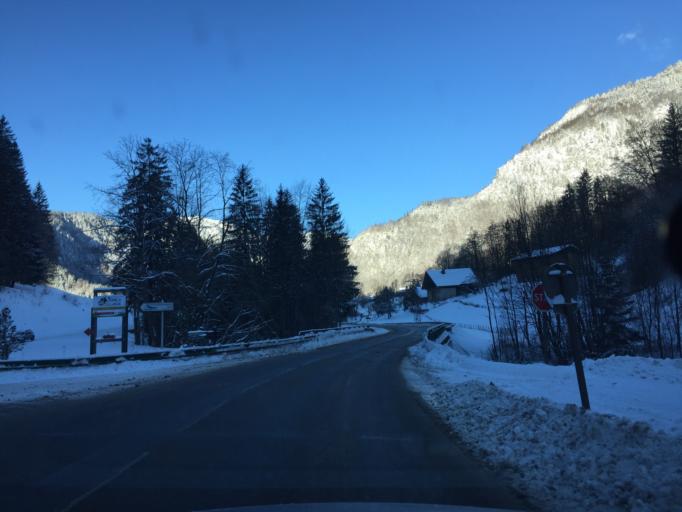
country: FR
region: Rhone-Alpes
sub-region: Departement de la Haute-Savoie
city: Abondance
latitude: 46.2816
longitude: 6.7066
